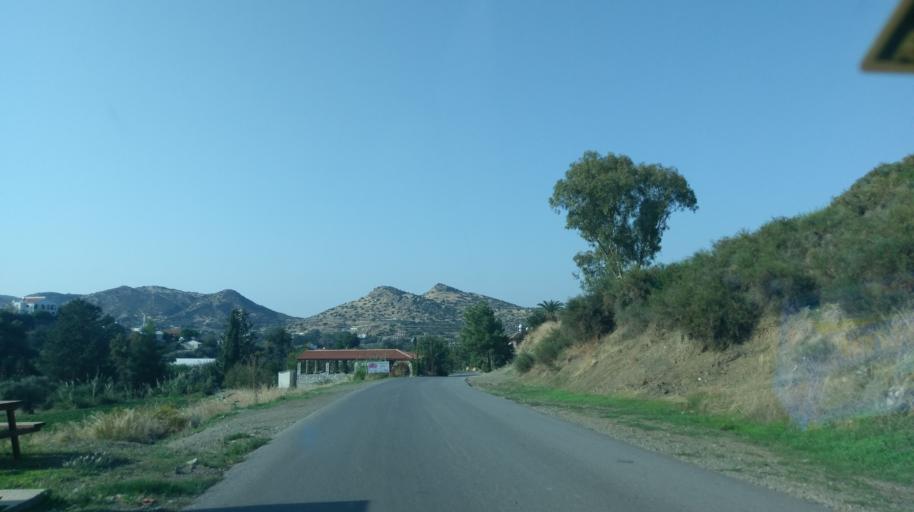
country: CY
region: Lefkosia
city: Kato Pyrgos
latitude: 35.1648
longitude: 32.7483
